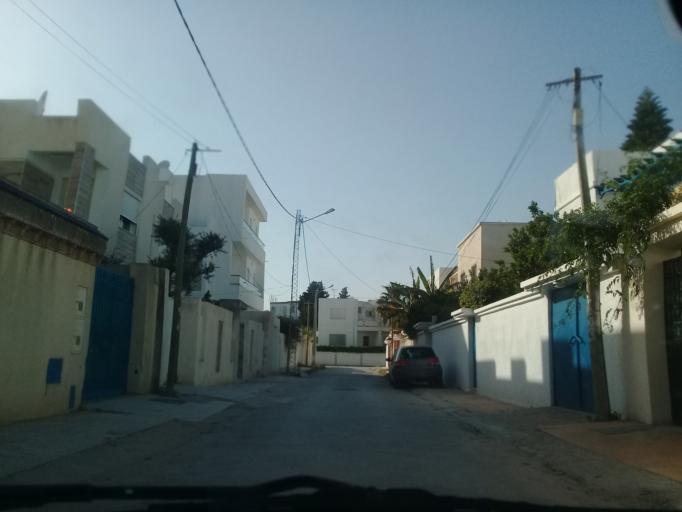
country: TN
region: Ariana
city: Ariana
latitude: 36.8361
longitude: 10.1964
